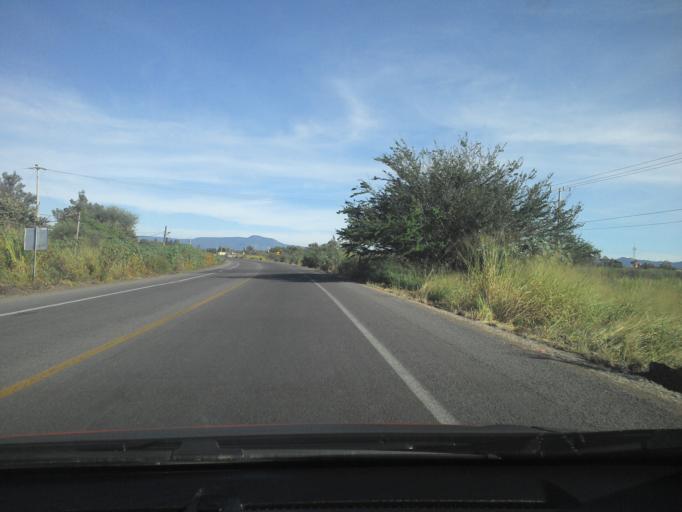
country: MX
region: Jalisco
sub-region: Teuchitlan
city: La Estanzuela
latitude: 20.6746
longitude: -103.8311
